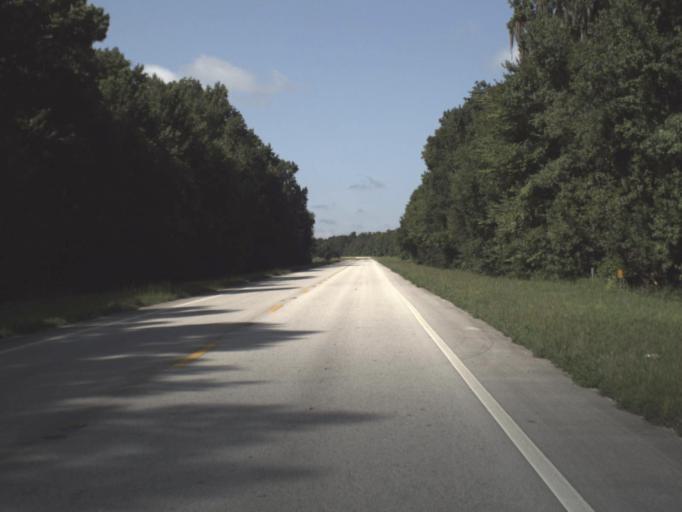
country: US
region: Florida
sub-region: Hernando County
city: North Brooksville
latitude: 28.6054
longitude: -82.4110
